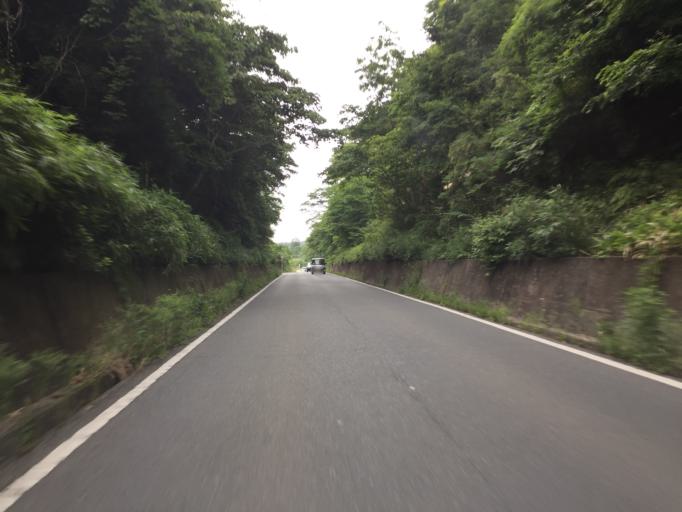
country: JP
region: Miyagi
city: Marumori
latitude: 37.7748
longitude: 140.9360
